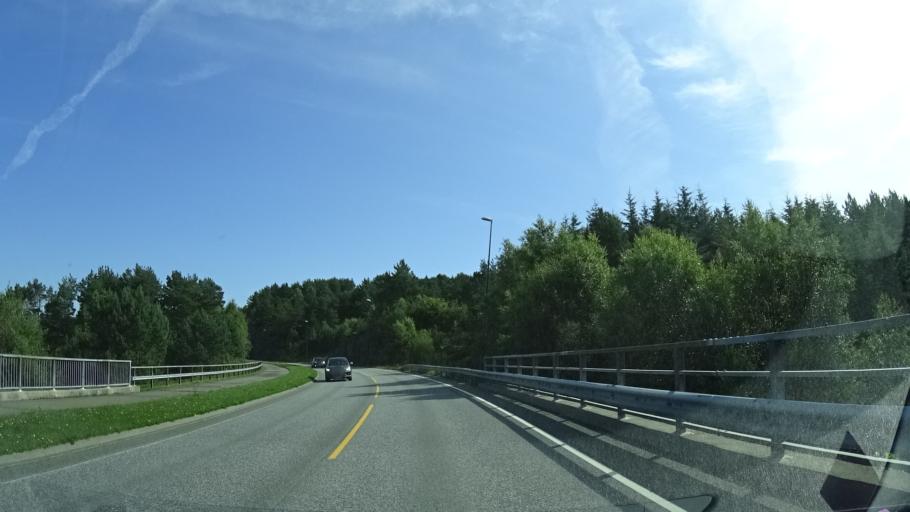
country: NO
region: Hordaland
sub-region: Bomlo
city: Mosterhamn
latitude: 59.7321
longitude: 5.3586
